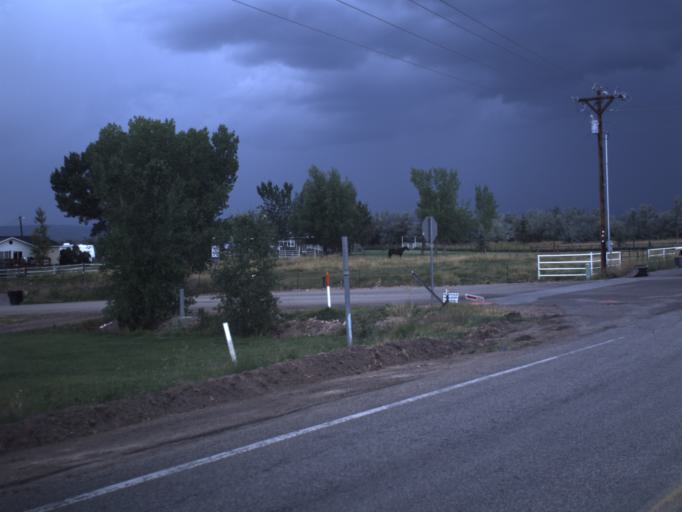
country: US
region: Utah
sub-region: Duchesne County
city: Roosevelt
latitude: 40.3598
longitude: -110.0296
